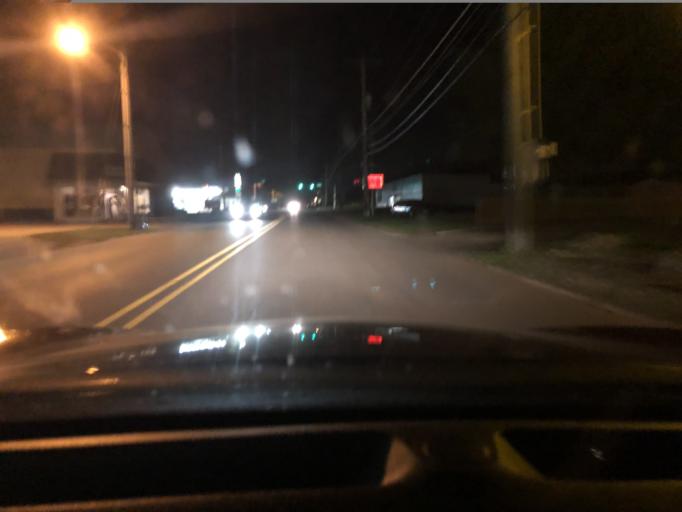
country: US
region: Indiana
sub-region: DeKalb County
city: Auburn
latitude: 41.3537
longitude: -85.0589
